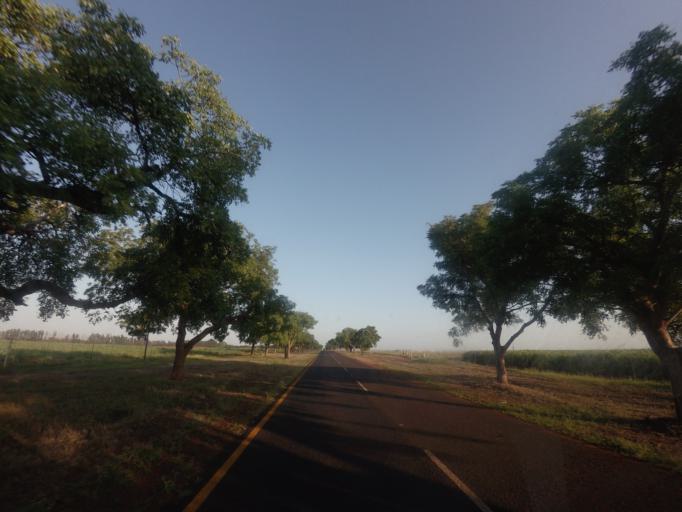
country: ZA
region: Mpumalanga
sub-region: Ehlanzeni District
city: Komatipoort
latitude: -25.3812
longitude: 31.9092
